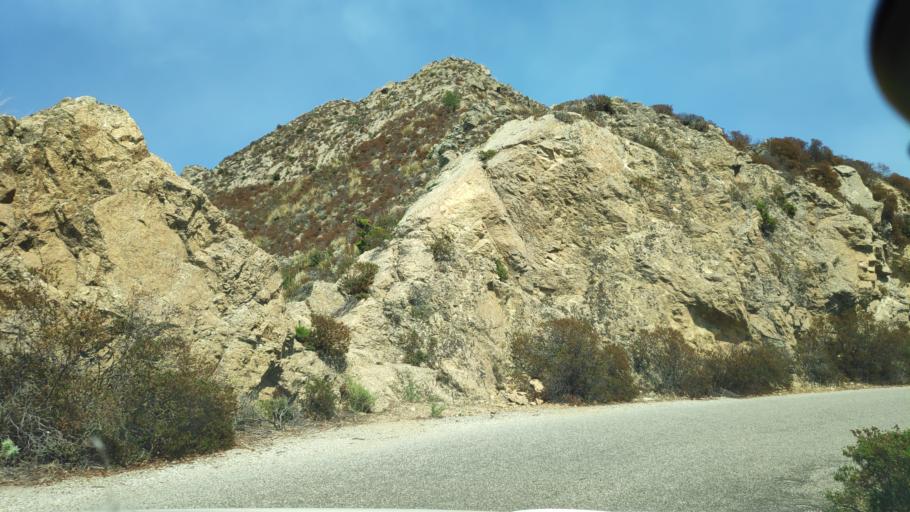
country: IT
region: Calabria
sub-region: Provincia di Reggio Calabria
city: Bova
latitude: 38.0008
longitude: 15.9229
